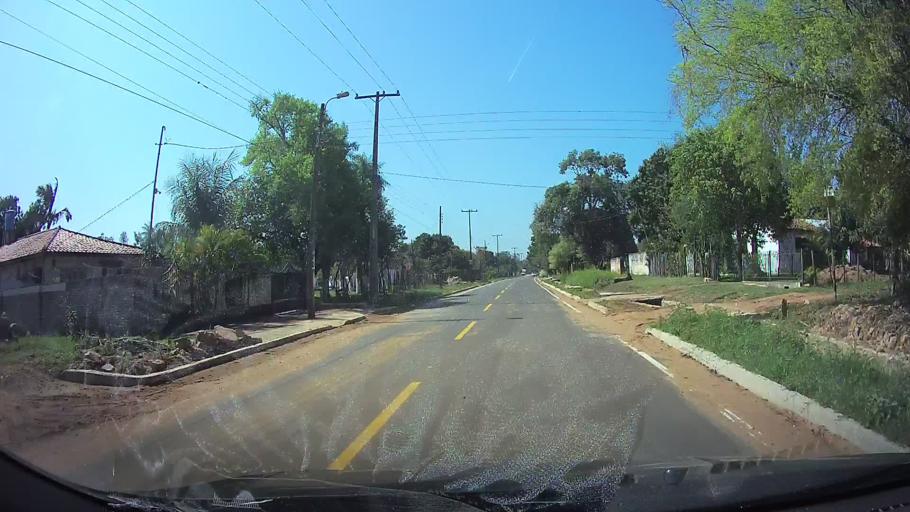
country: PY
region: Central
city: Limpio
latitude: -25.2238
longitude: -57.4874
